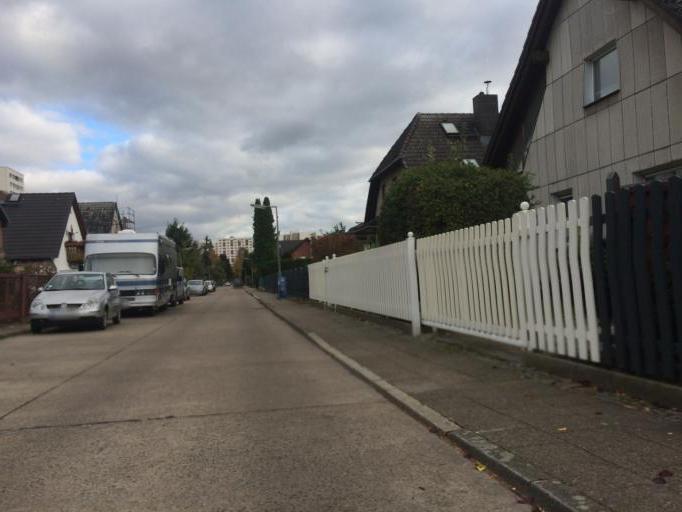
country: DE
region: Berlin
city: Markisches Viertel
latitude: 52.5948
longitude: 13.3525
